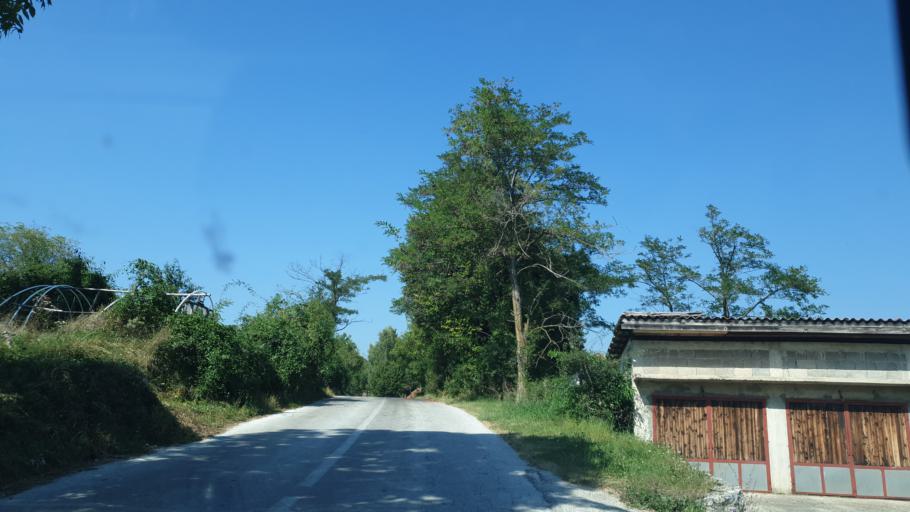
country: RS
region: Central Serbia
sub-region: Zlatiborski Okrug
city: Cajetina
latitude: 43.6867
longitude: 19.8479
